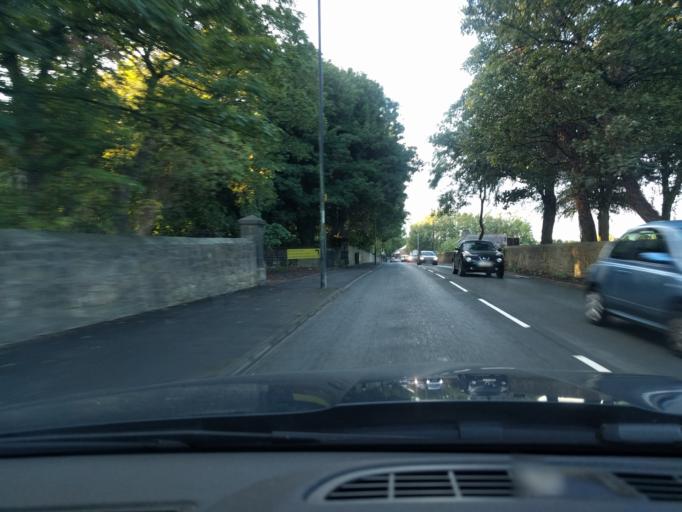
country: GB
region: England
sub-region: Northumberland
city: Backworth
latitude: 55.0387
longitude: -1.5266
